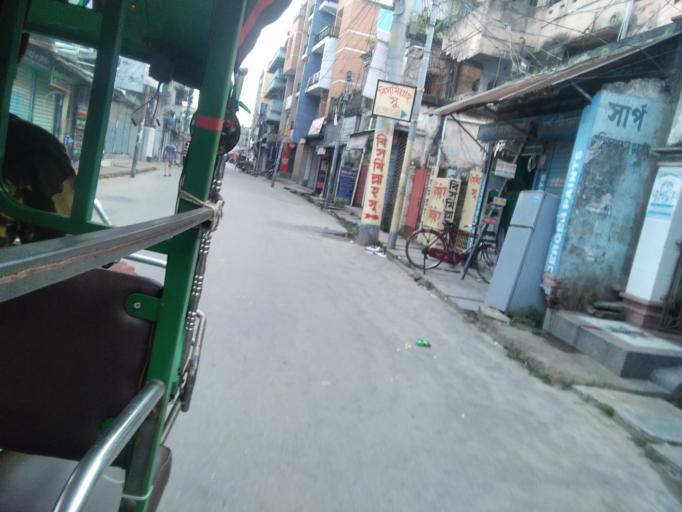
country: BD
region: Khulna
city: Khulna
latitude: 22.8141
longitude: 89.5617
